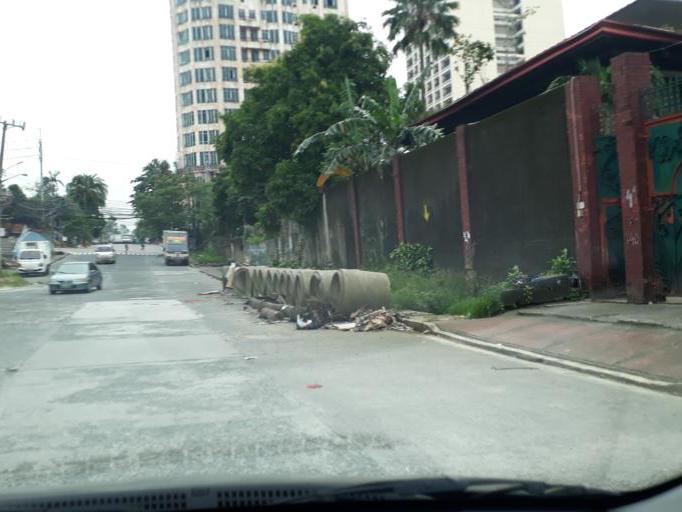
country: PH
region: Metro Manila
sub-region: Quezon City
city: Quezon City
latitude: 14.6414
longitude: 121.0354
